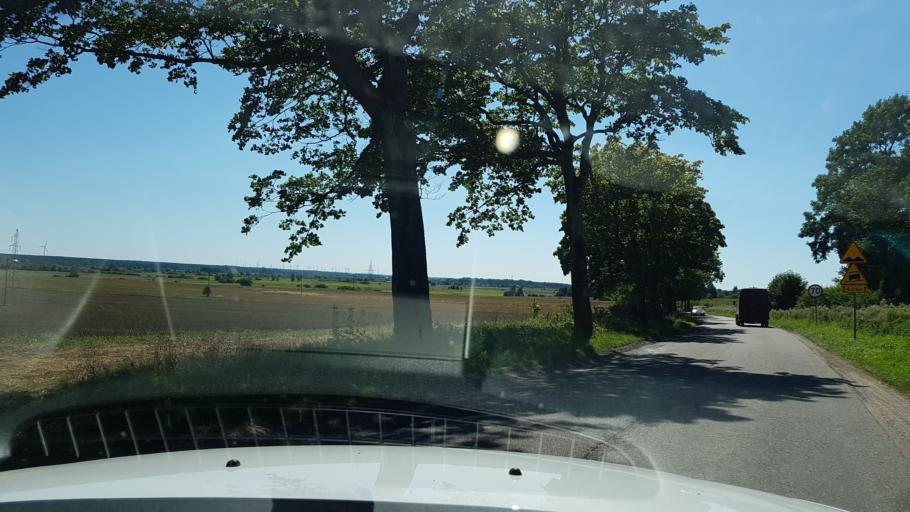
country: PL
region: West Pomeranian Voivodeship
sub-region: Powiat slawienski
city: Darlowo
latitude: 54.4553
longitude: 16.4898
